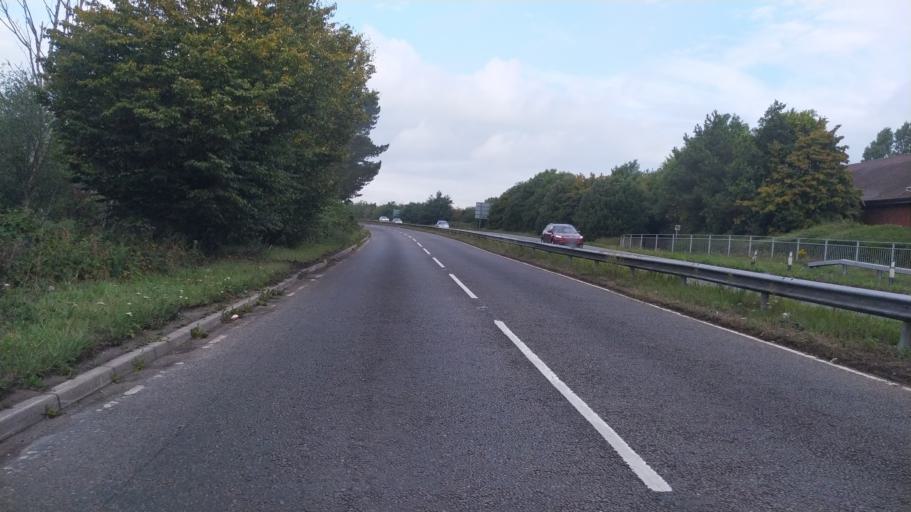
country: GB
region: England
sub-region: Hampshire
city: Bransgore
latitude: 50.7435
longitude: -1.7421
